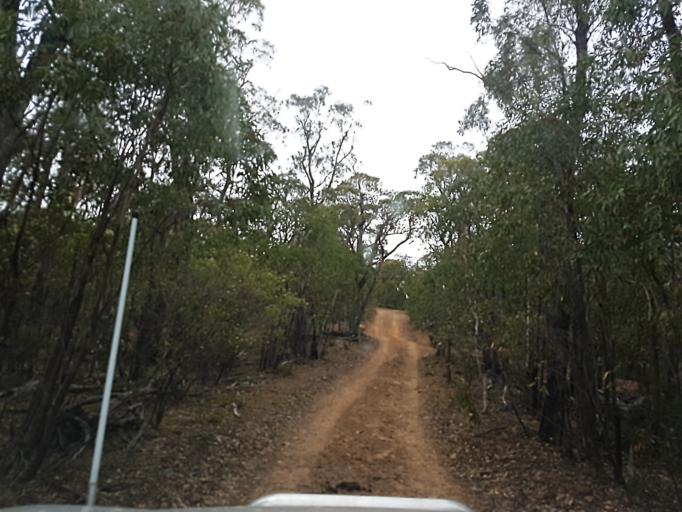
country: AU
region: New South Wales
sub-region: Snowy River
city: Jindabyne
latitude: -36.8622
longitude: 148.2650
